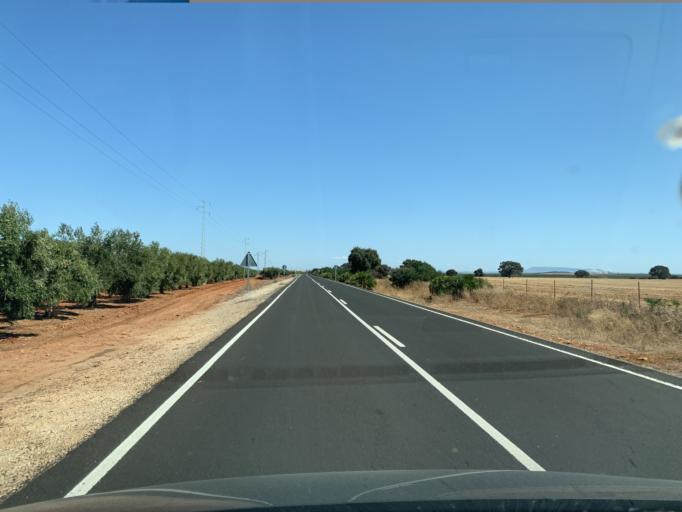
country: ES
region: Andalusia
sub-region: Provincia de Sevilla
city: La Lantejuela
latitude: 37.3333
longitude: -5.3047
